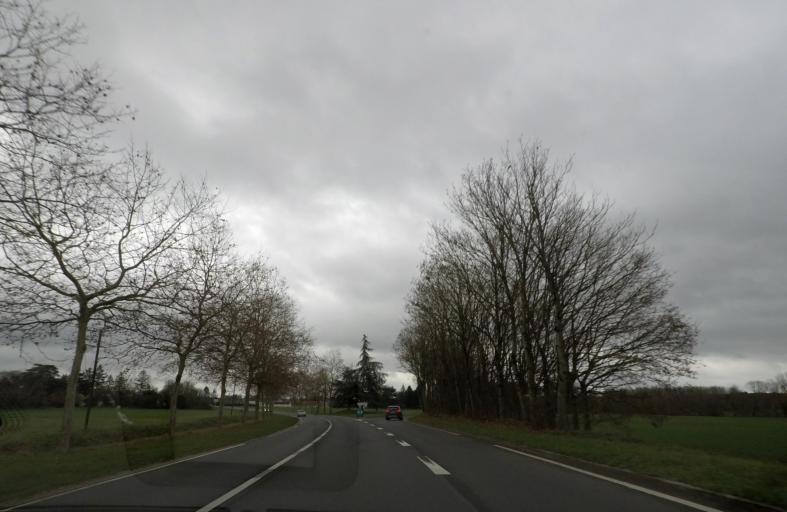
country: FR
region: Centre
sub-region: Departement du Loir-et-Cher
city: Cour-Cheverny
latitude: 47.5183
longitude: 1.4409
